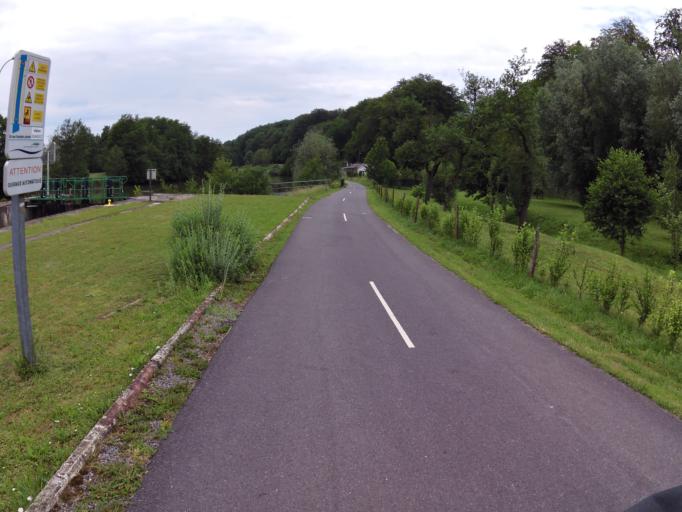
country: FR
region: Champagne-Ardenne
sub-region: Departement des Ardennes
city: Saint-Laurent
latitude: 49.7534
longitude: 4.7602
